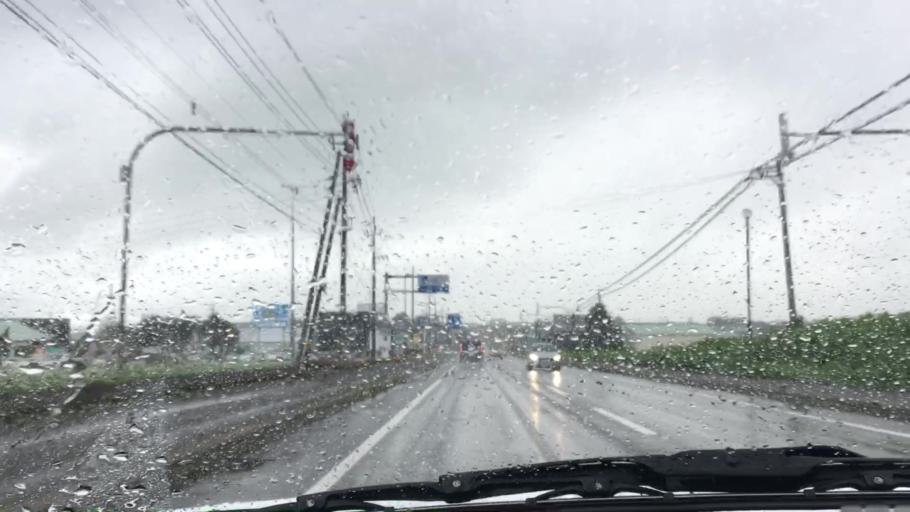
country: JP
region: Hokkaido
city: Niseko Town
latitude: 42.7416
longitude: 140.8864
